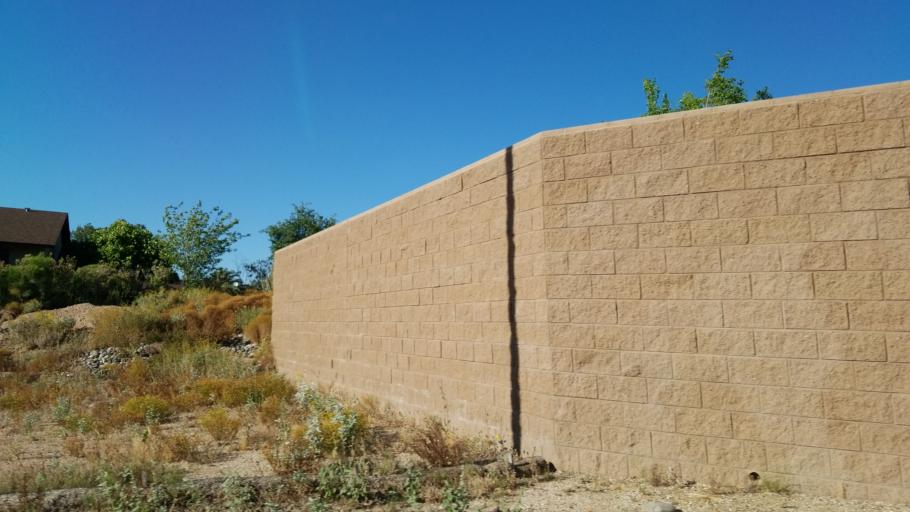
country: US
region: Arizona
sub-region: Maricopa County
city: Youngtown
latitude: 33.5802
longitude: -112.3050
